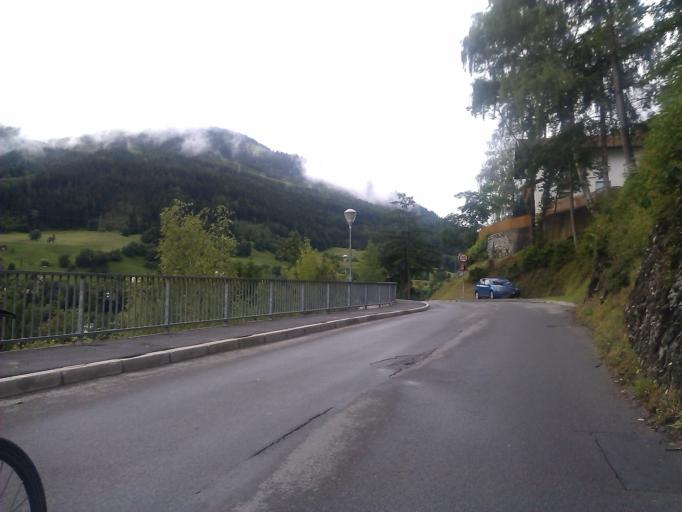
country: AT
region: Tyrol
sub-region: Politischer Bezirk Landeck
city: Landeck
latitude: 47.1448
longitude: 10.5649
